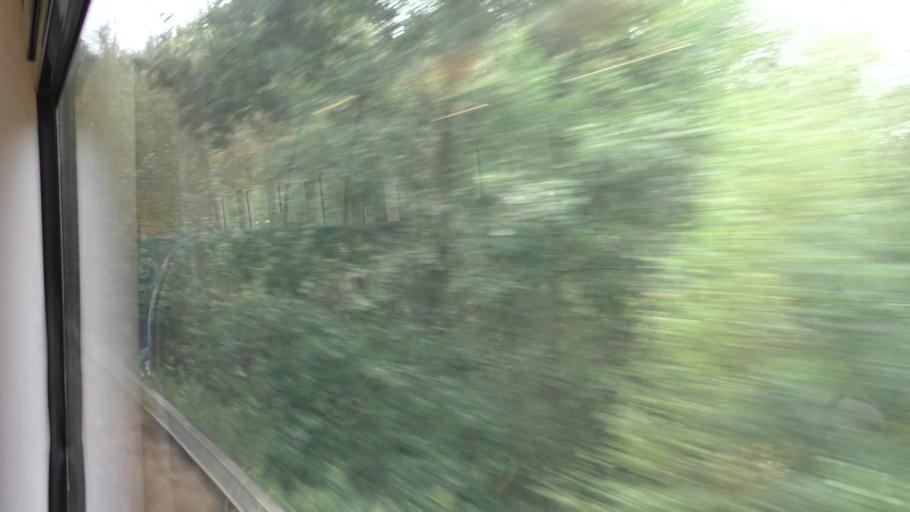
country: DE
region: Saxony
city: Goerlitz
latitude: 51.1159
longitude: 14.9686
